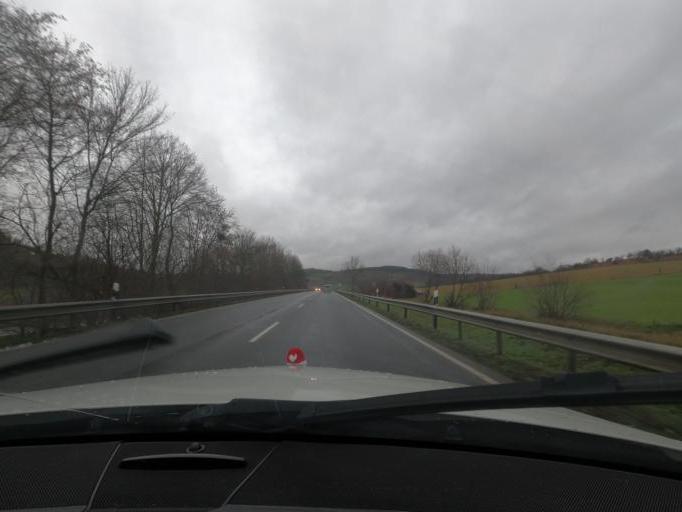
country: DE
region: Lower Saxony
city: Einbeck
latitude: 51.8026
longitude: 9.9206
